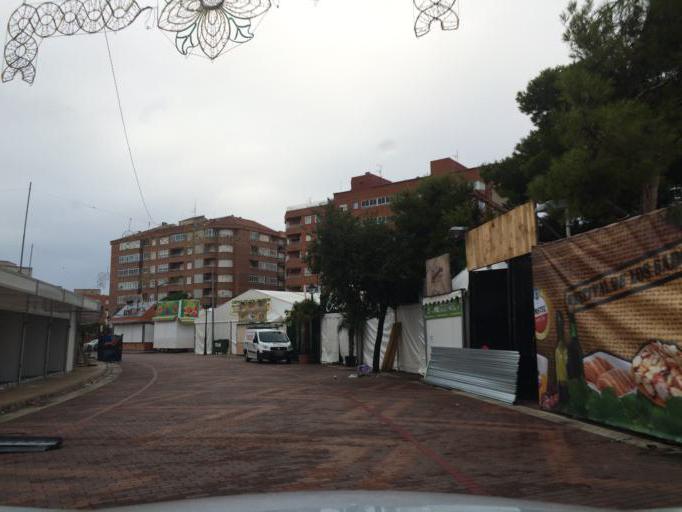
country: ES
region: Castille-La Mancha
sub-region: Provincia de Albacete
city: Albacete
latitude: 38.9979
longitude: -1.8709
